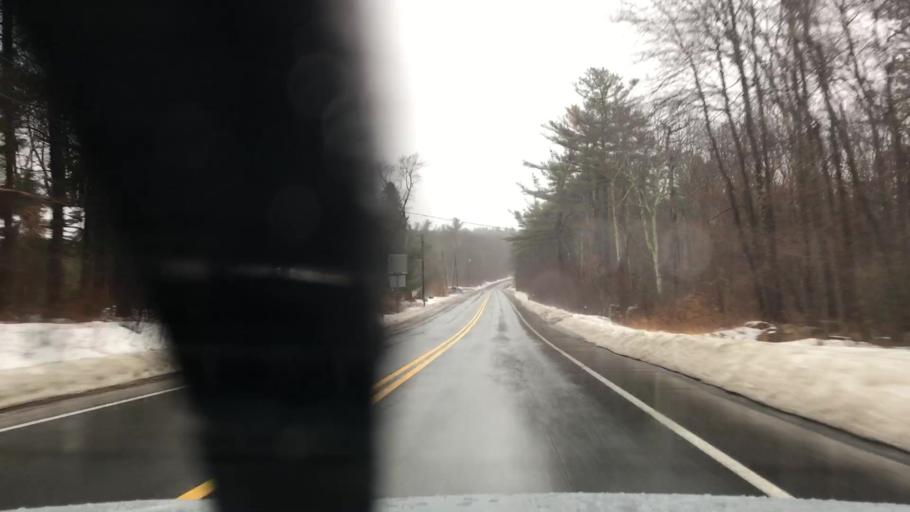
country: US
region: Massachusetts
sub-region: Hampshire County
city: Pelham
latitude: 42.3937
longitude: -72.4037
